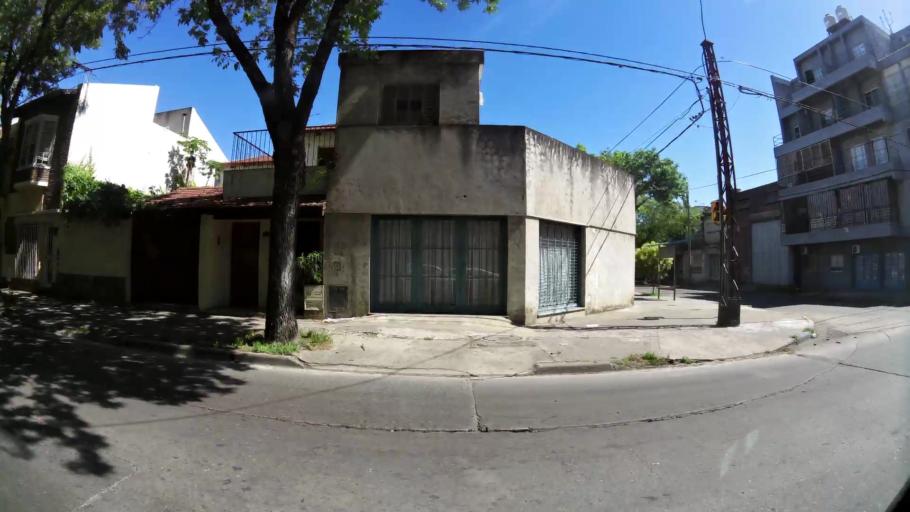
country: AR
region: Santa Fe
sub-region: Departamento de Rosario
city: Rosario
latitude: -32.9412
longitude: -60.6895
